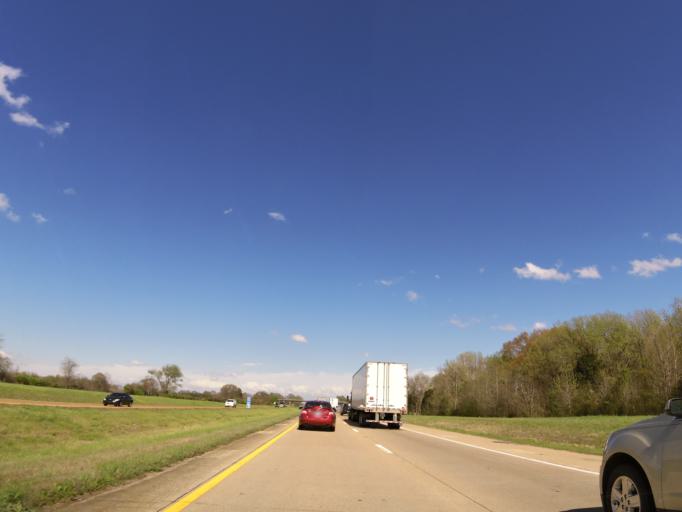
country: US
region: Tennessee
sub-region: Gibson County
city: Medina
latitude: 35.7115
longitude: -88.6552
